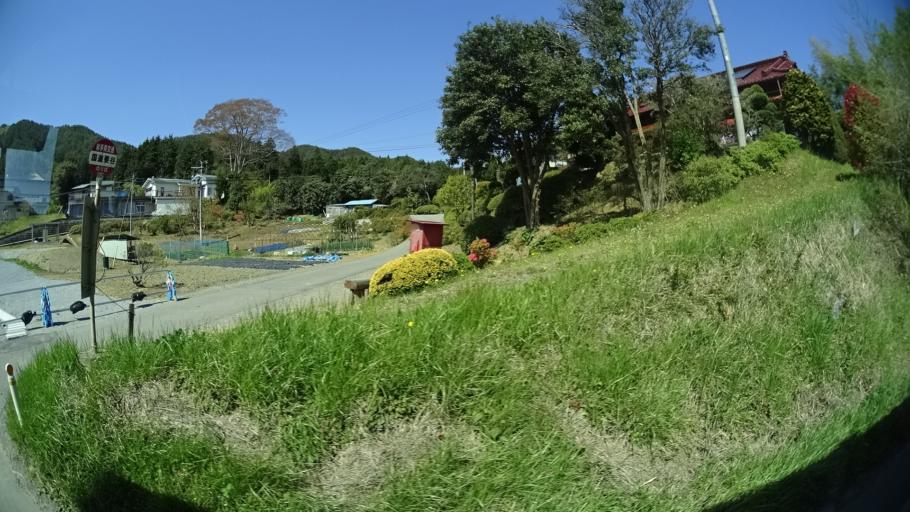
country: JP
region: Iwate
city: Ofunato
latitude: 38.9820
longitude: 141.6213
